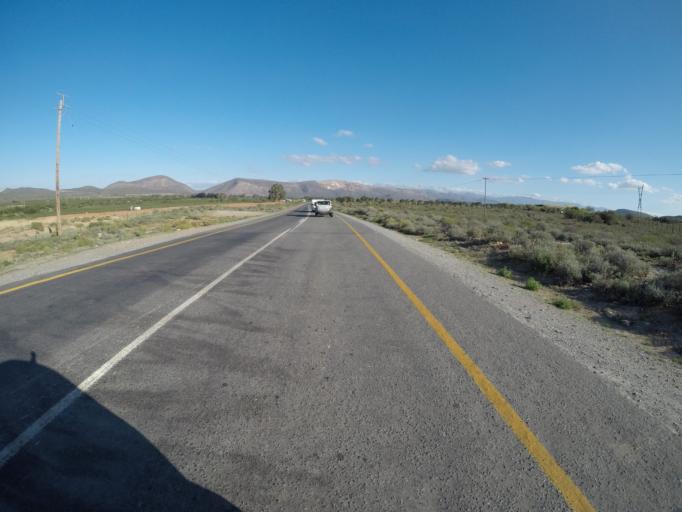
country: ZA
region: Western Cape
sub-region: Cape Winelands District Municipality
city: Ashton
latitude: -33.7910
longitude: 19.7794
